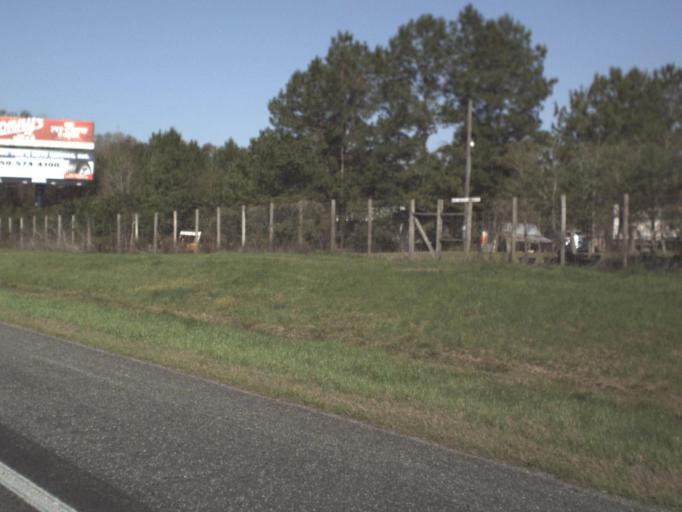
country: US
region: Florida
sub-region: Jefferson County
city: Monticello
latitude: 30.4895
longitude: -84.0158
